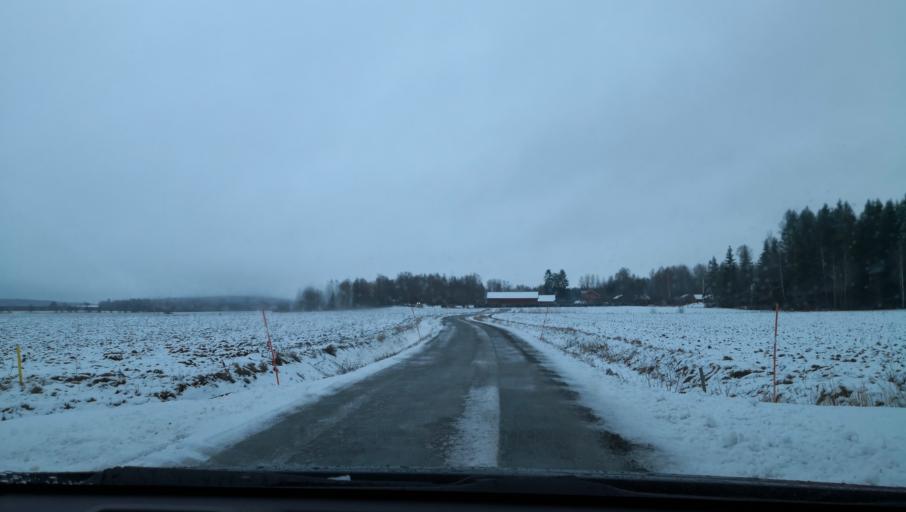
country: SE
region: Vaestmanland
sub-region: Kopings Kommun
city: Kolsva
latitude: 59.5539
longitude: 15.8748
